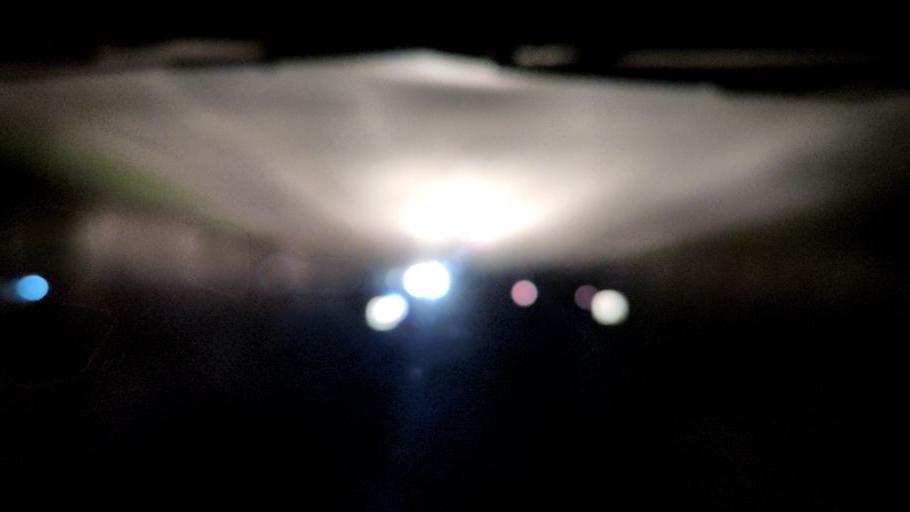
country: RU
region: Voronezj
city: Podkletnoye
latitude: 51.6229
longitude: 39.5430
